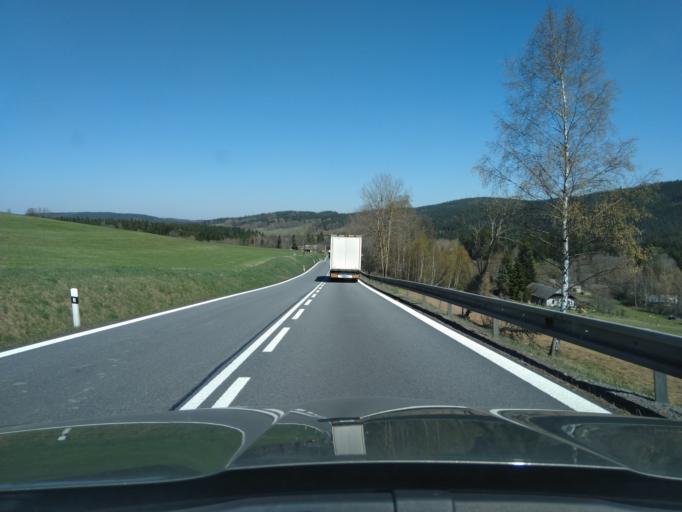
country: CZ
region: Jihocesky
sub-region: Okres Prachatice
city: Vimperk
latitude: 49.0096
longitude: 13.7678
